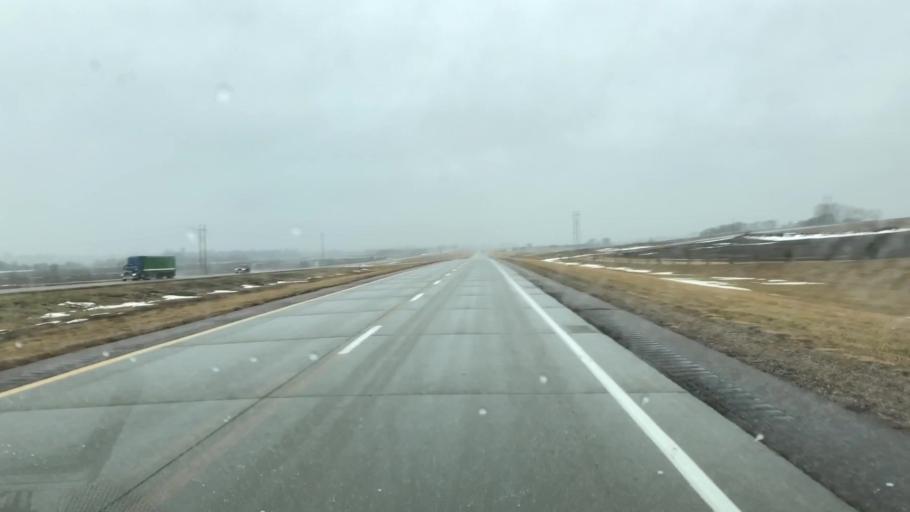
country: US
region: Iowa
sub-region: Sioux County
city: Orange City
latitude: 42.8978
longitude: -96.0882
